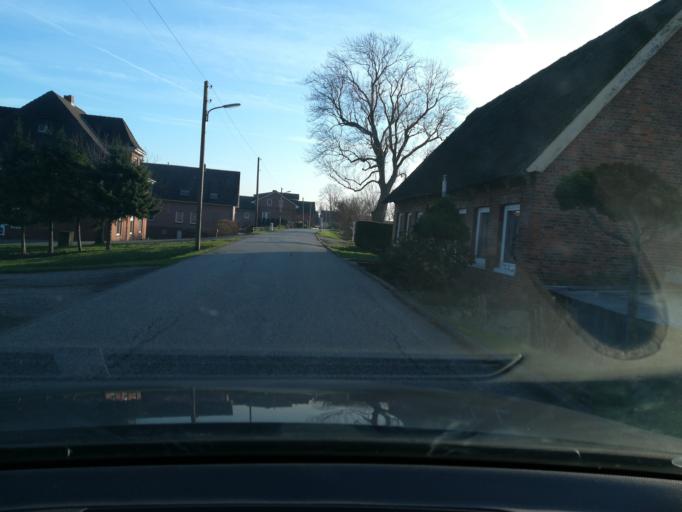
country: DE
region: Lower Saxony
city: Stelle
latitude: 53.4451
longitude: 10.1099
